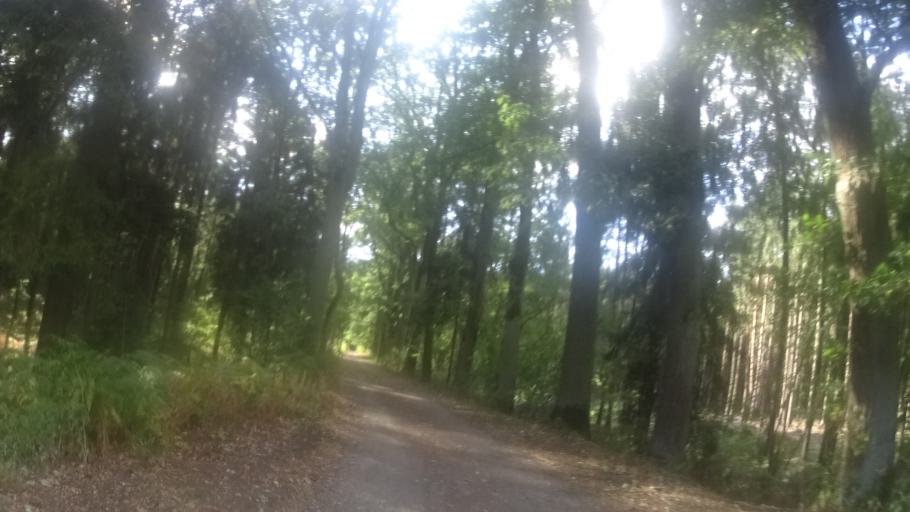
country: CZ
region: Kralovehradecky
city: Trebechovice pod Orebem
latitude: 50.1778
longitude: 16.0340
